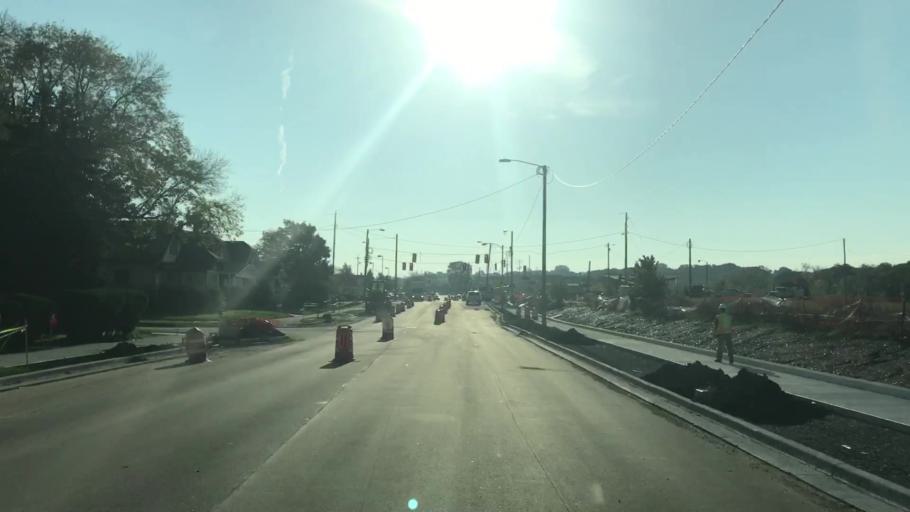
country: US
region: Wisconsin
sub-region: Milwaukee County
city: Wauwatosa
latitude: 43.0477
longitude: -88.0015
